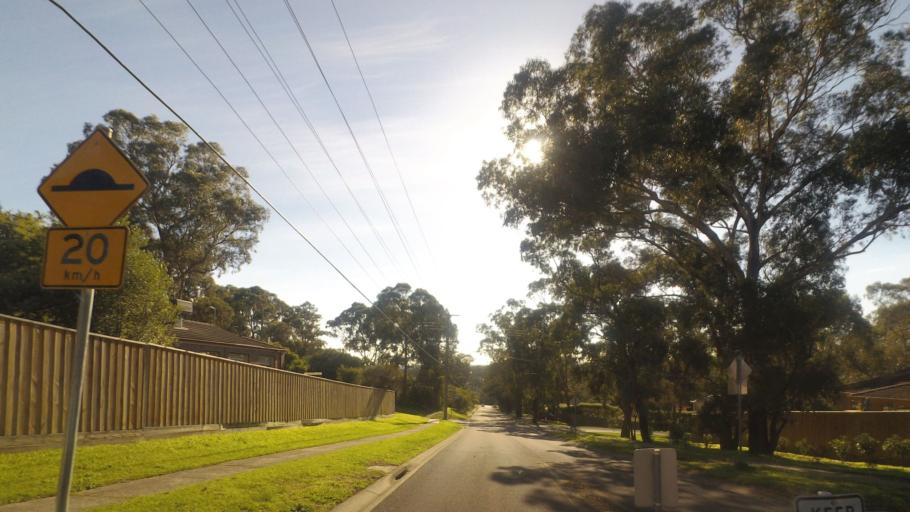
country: AU
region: Victoria
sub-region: Nillumbik
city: Eltham North
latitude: -37.7078
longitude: 145.1615
